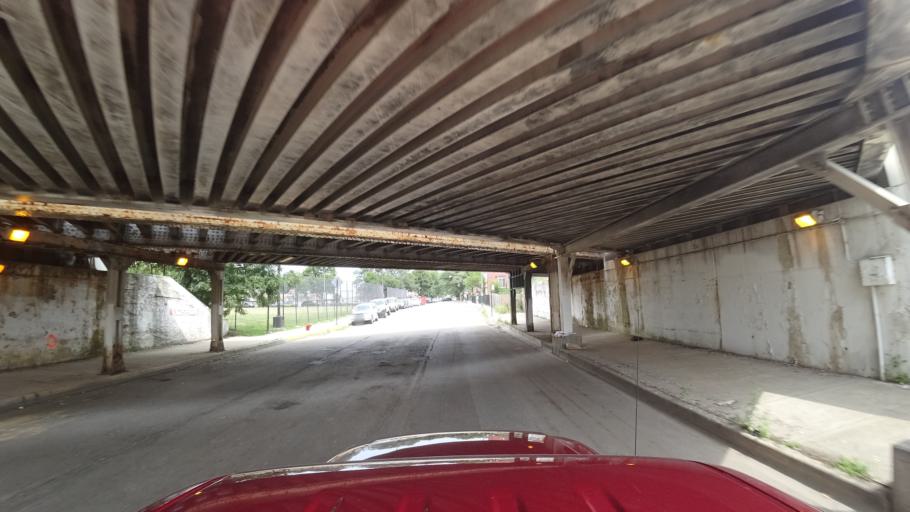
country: US
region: Illinois
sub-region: Cook County
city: Chicago
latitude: 41.8311
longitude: -87.6778
